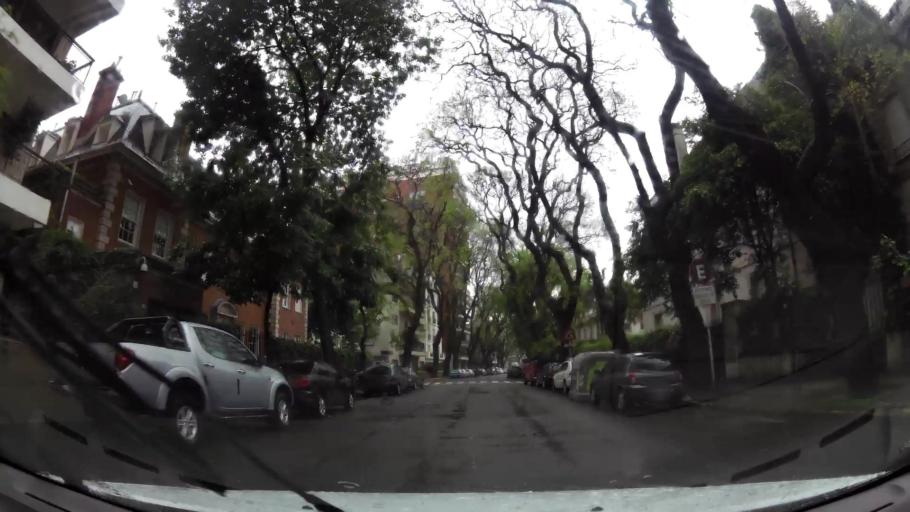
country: AR
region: Buenos Aires F.D.
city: Retiro
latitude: -34.5796
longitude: -58.4030
